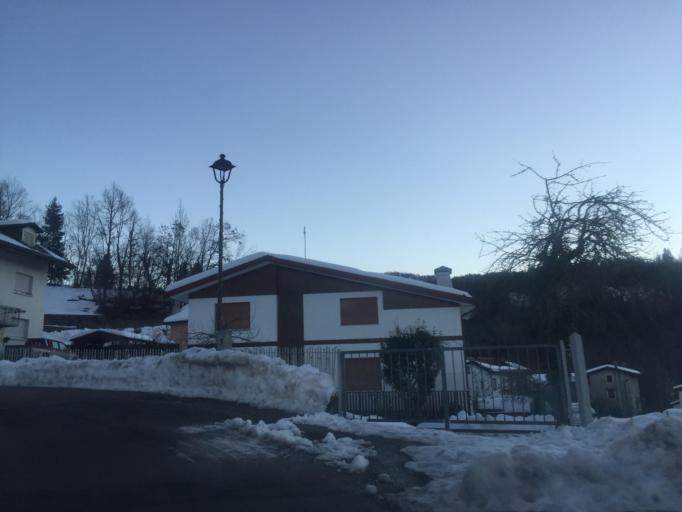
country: IT
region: Friuli Venezia Giulia
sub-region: Provincia di Udine
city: Lauco
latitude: 46.4261
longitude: 12.9329
